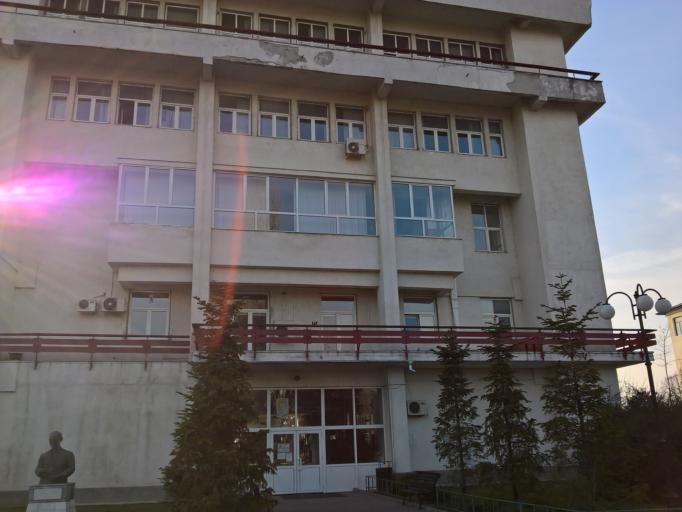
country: RO
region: Bucuresti
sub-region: Municipiul Bucuresti
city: Bucuresti
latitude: 44.4705
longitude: 26.0688
